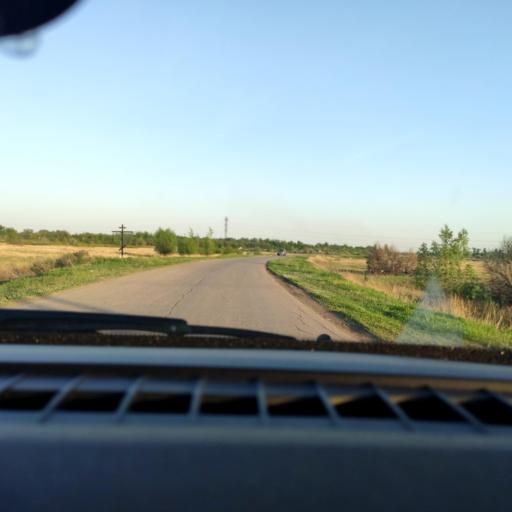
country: RU
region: Samara
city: Georgiyevka
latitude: 53.2686
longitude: 50.9600
